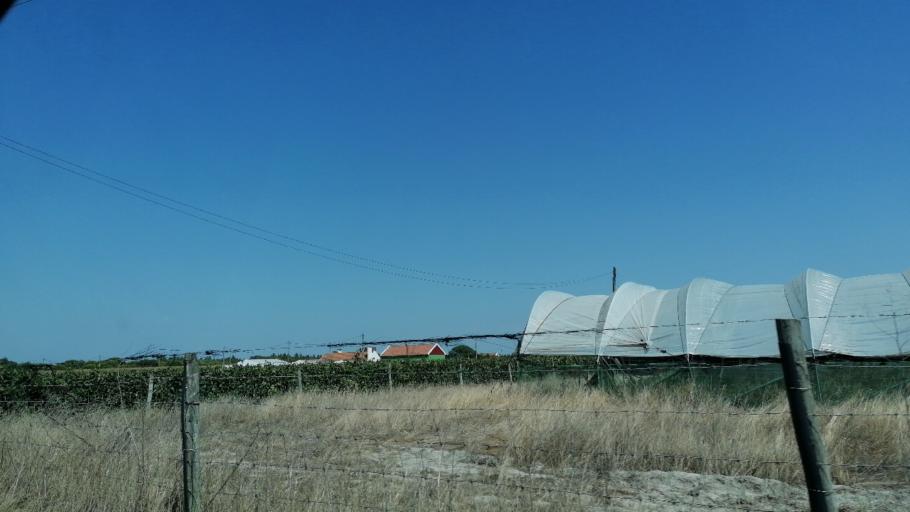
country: PT
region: Santarem
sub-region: Benavente
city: Poceirao
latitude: 38.7198
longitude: -8.7105
